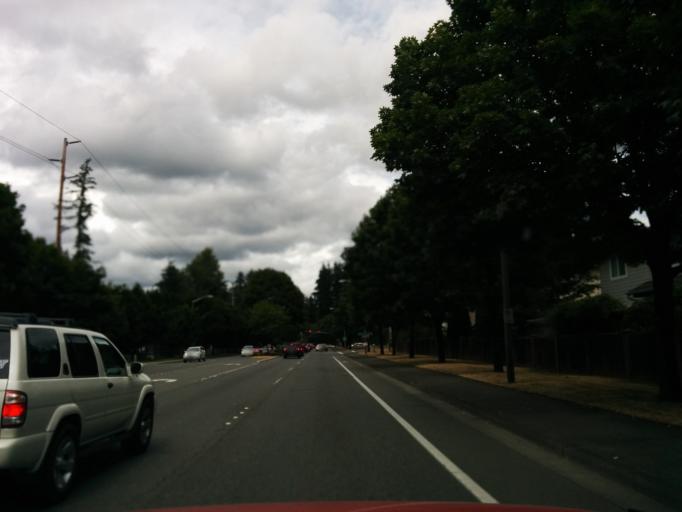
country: US
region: Washington
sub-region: King County
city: Redmond
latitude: 47.6831
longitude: -122.0988
